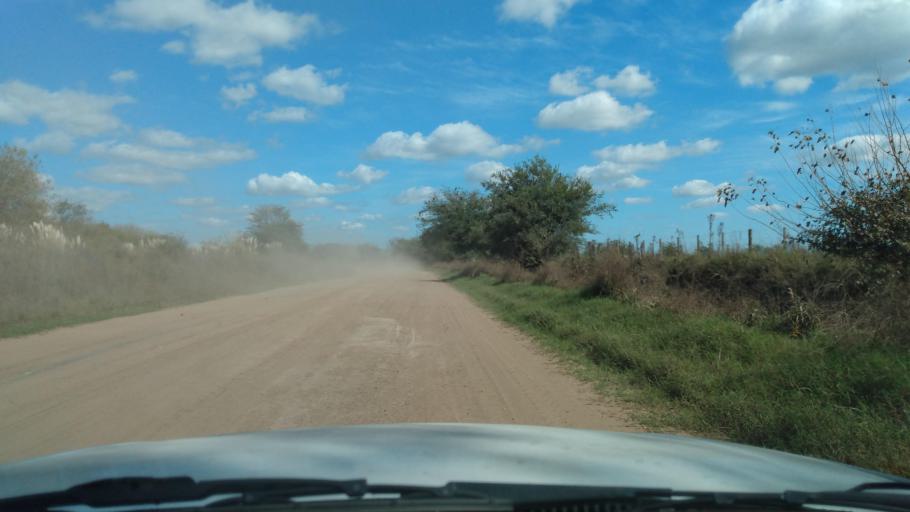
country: AR
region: Buenos Aires
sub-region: Partido de Navarro
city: Navarro
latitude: -35.0161
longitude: -59.4231
